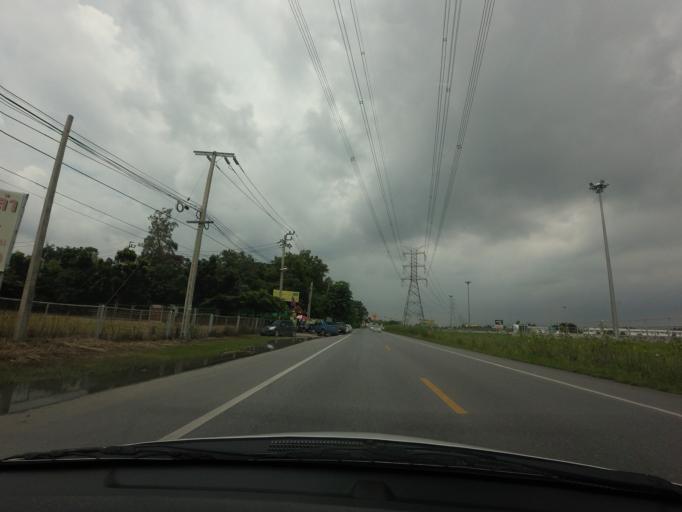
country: TH
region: Bangkok
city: Saphan Sung
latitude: 13.7388
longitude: 100.7020
